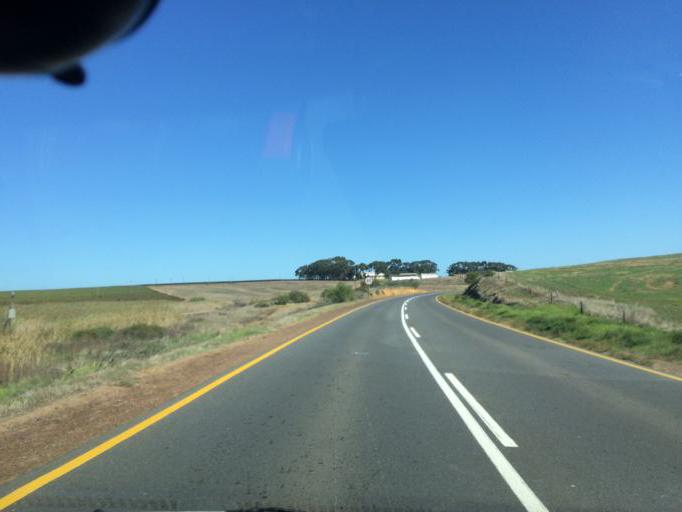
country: ZA
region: Western Cape
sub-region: City of Cape Town
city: Atlantis
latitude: -33.6665
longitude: 18.5678
